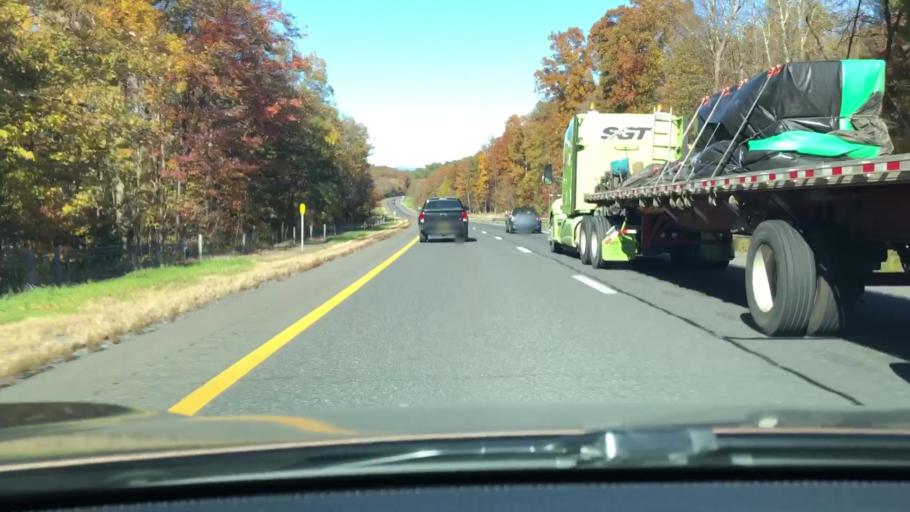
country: US
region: New York
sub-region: Ulster County
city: Tillson
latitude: 41.7878
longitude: -74.0499
